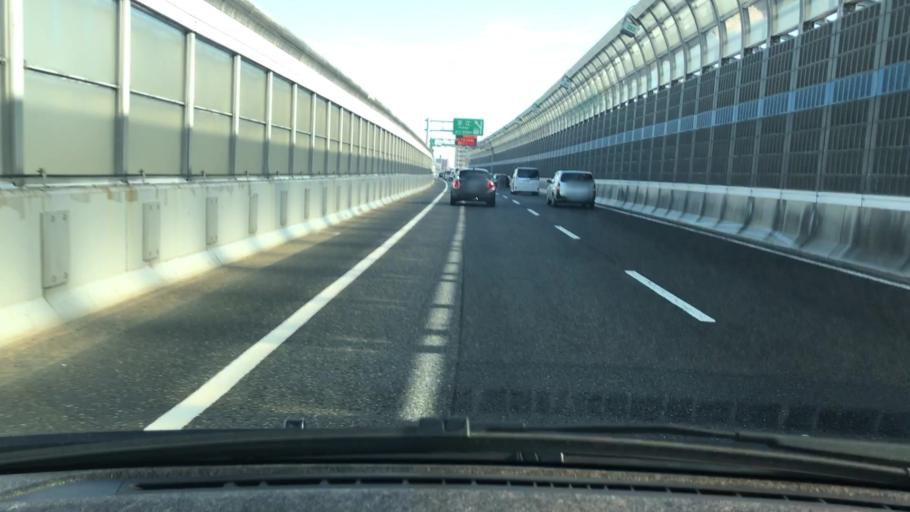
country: JP
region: Hyogo
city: Ashiya
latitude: 34.7139
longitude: 135.2779
